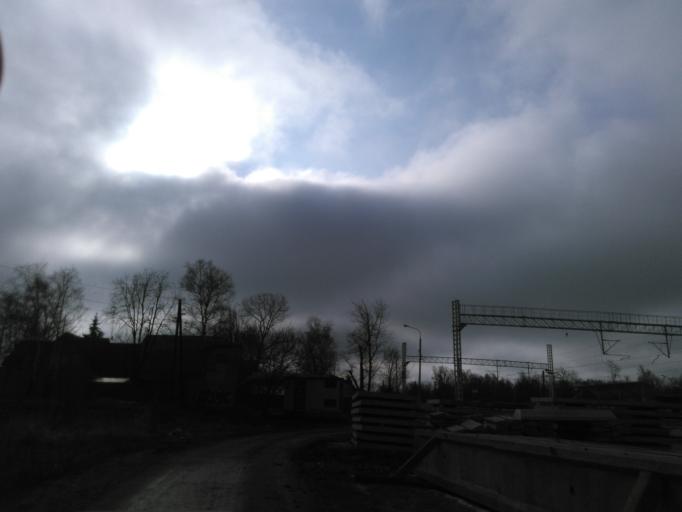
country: RU
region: Moskovskaya
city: Novopodrezkovo
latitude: 55.9249
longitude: 37.3811
